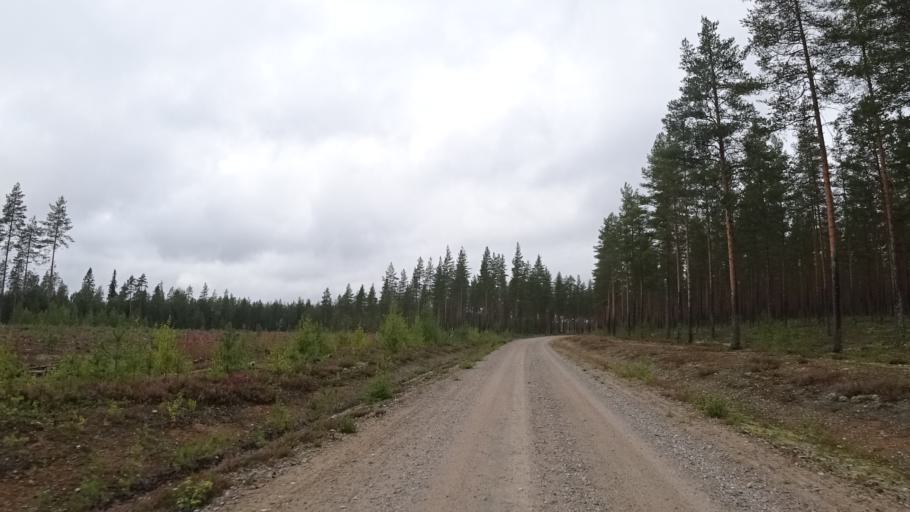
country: FI
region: North Karelia
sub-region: Pielisen Karjala
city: Lieksa
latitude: 63.5205
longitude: 30.1013
